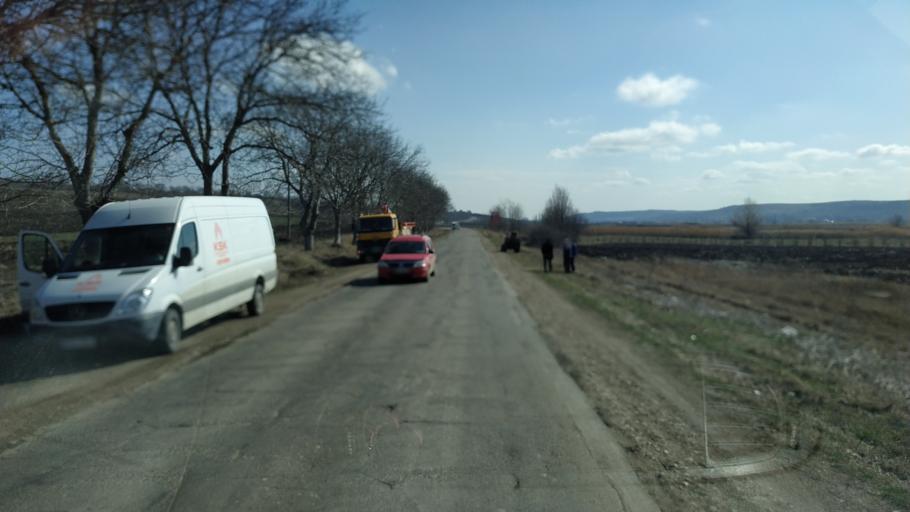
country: MD
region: Laloveni
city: Ialoveni
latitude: 46.9266
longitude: 28.6773
